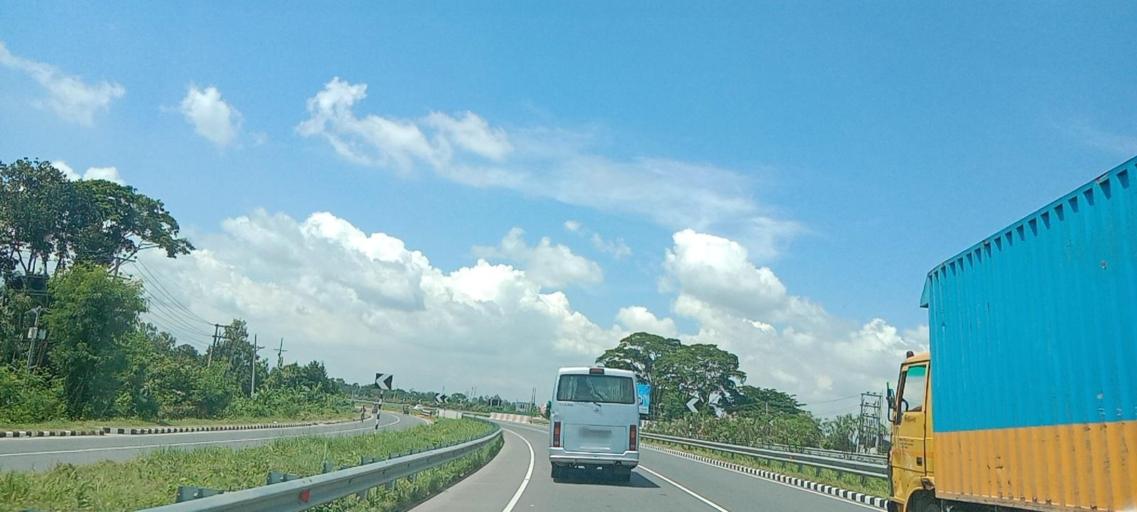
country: BD
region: Dhaka
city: Dohar
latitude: 23.5478
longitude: 90.2994
